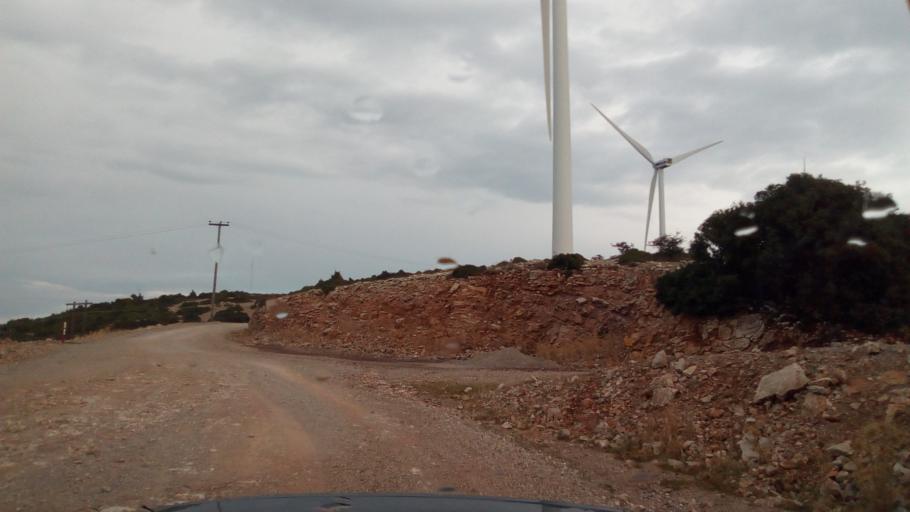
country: GR
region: West Greece
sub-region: Nomos Achaias
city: Kamarai
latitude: 38.4207
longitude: 22.0396
